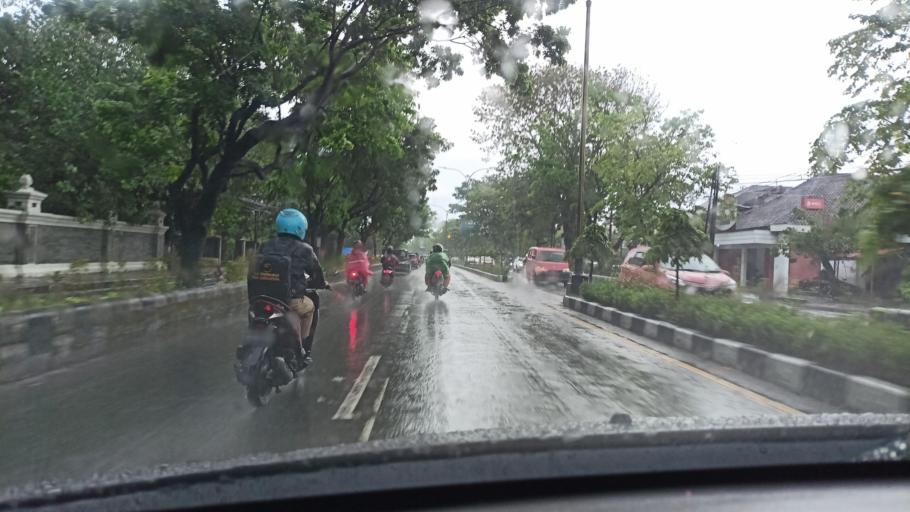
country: ID
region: Central Java
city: Colomadu
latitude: -7.5479
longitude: 110.7814
